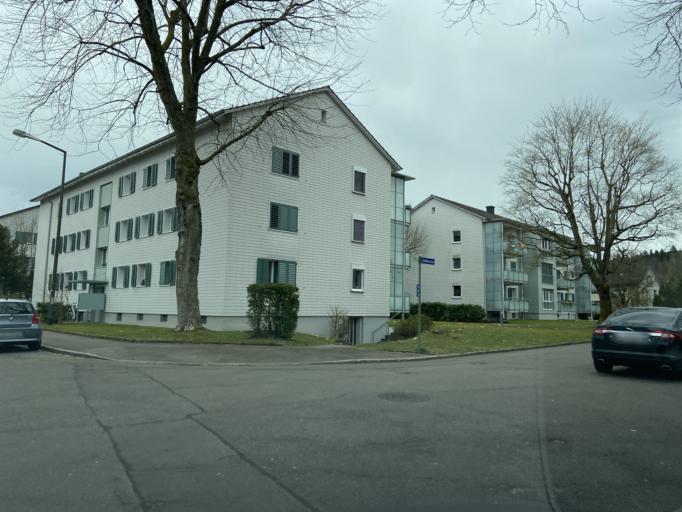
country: CH
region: Zurich
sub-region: Bezirk Winterthur
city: Mattenbach (Kreis 7)
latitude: 47.4903
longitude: 8.7435
